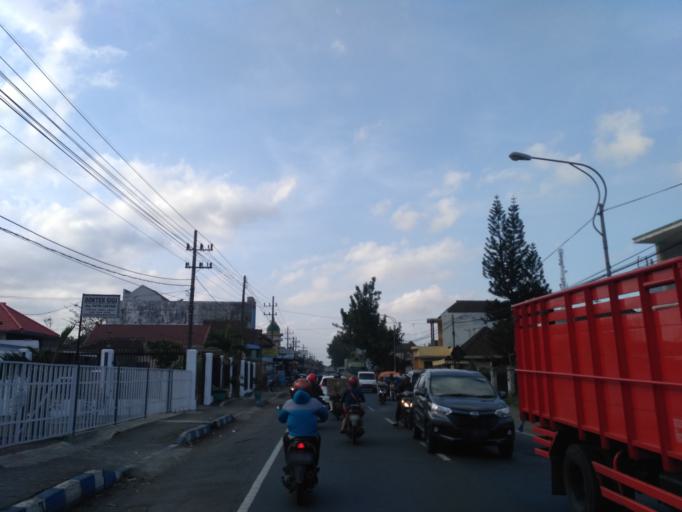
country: ID
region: East Java
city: Pakisaji
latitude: -8.0668
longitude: 112.5983
